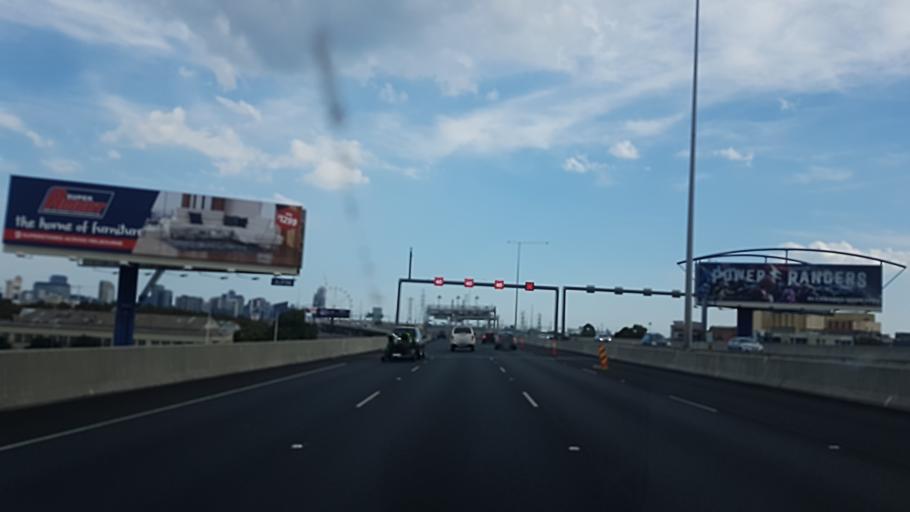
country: AU
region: Victoria
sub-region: Moonee Valley
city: Flemington
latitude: -37.7937
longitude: 144.9364
